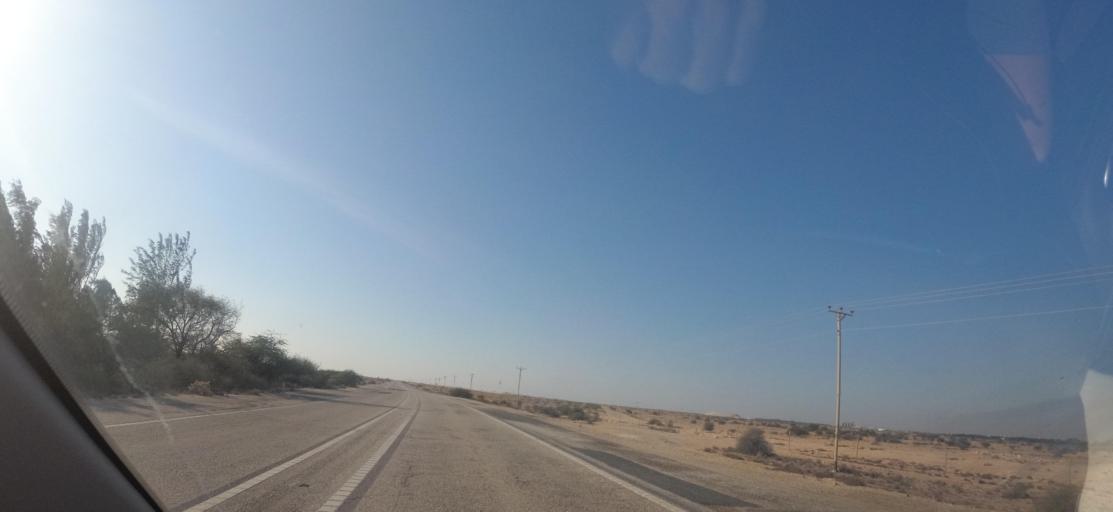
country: QA
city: Al Ghuwayriyah
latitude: 25.8563
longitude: 51.2545
